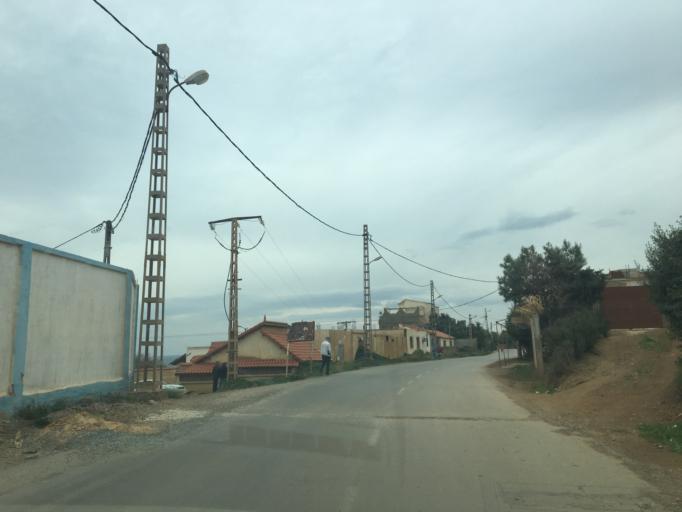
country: DZ
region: Tipaza
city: Tipasa
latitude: 36.6406
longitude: 2.3669
